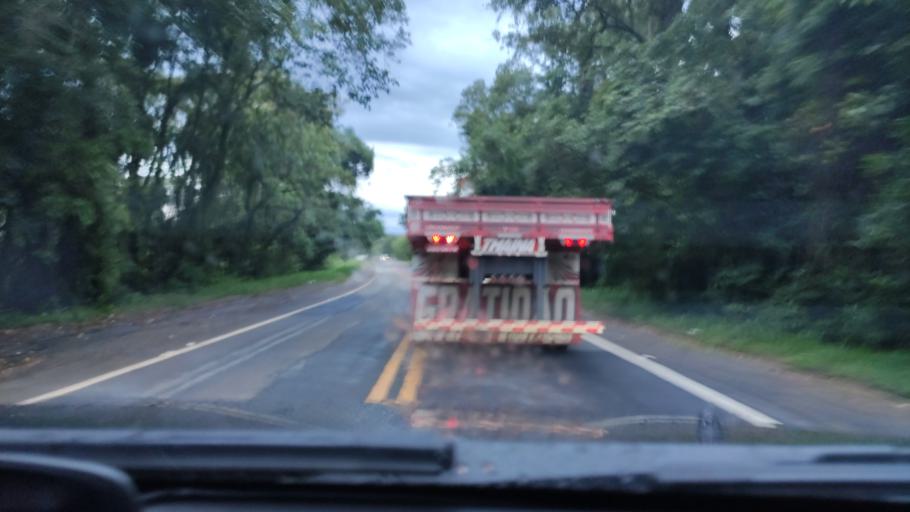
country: BR
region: Sao Paulo
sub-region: Socorro
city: Socorro
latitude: -22.7379
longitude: -46.5637
